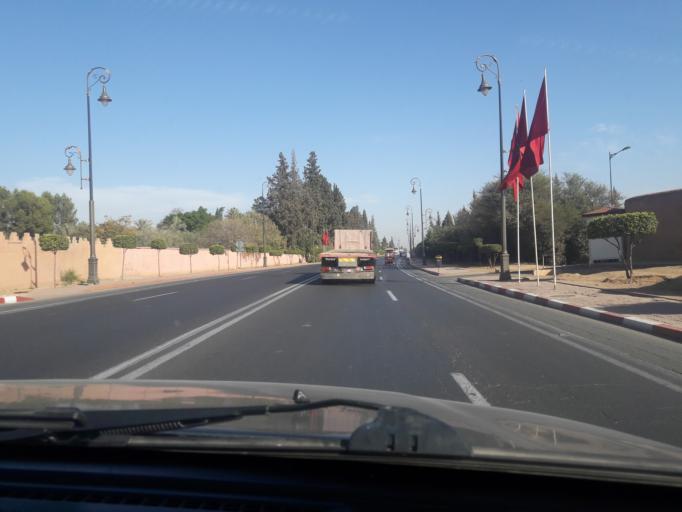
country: MA
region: Marrakech-Tensift-Al Haouz
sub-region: Marrakech
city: Marrakesh
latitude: 31.6483
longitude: -7.9627
